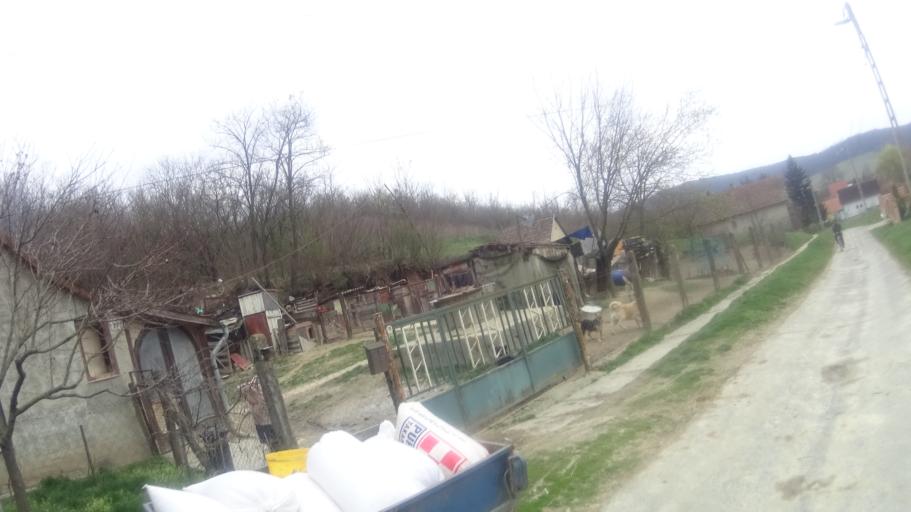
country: HU
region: Somogy
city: Adand
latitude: 46.8050
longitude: 18.0997
